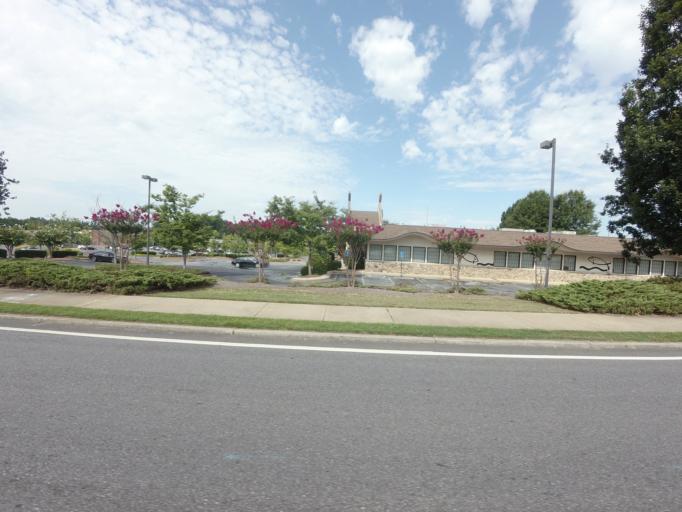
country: US
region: Georgia
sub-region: Fulton County
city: Johns Creek
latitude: 34.0461
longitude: -84.1766
